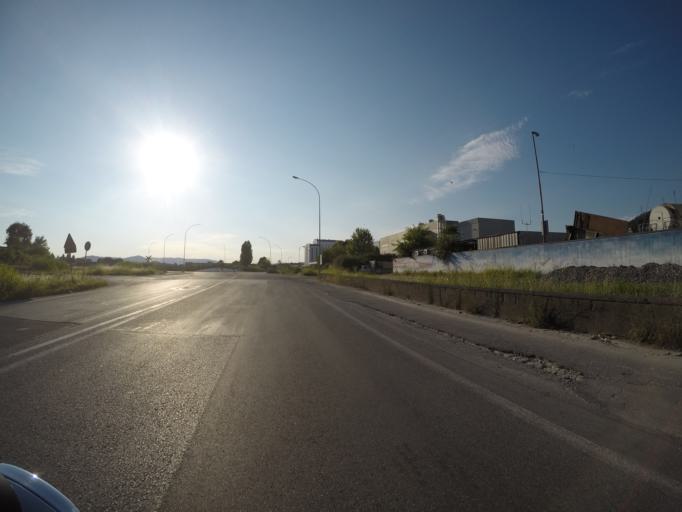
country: IT
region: Tuscany
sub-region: Provincia di Massa-Carrara
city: Carrara
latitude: 44.0397
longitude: 10.0804
